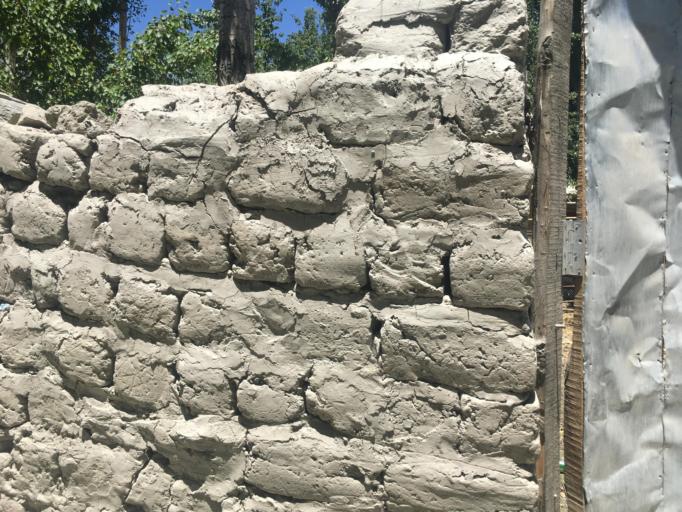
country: PK
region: Gilgit-Baltistan
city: Skardu
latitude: 35.3061
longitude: 75.5454
